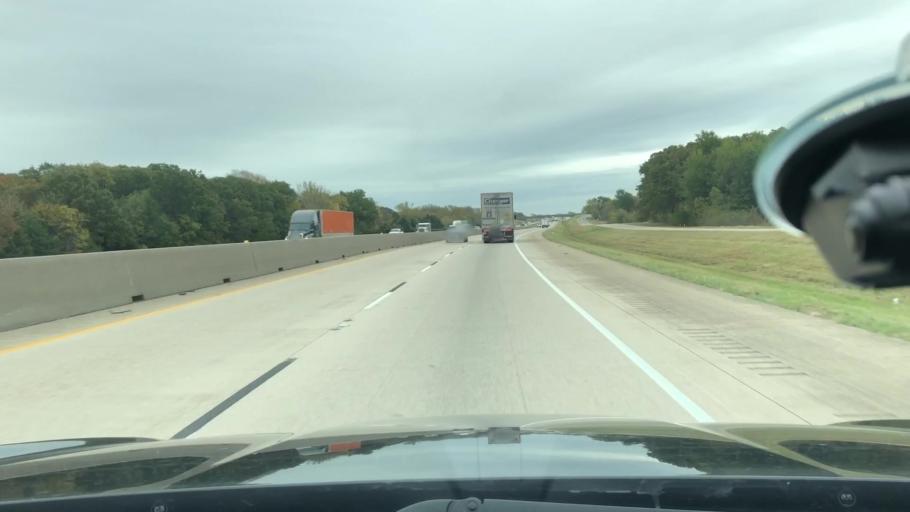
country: US
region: Texas
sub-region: Hopkins County
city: Sulphur Springs
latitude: 33.1263
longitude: -95.7428
